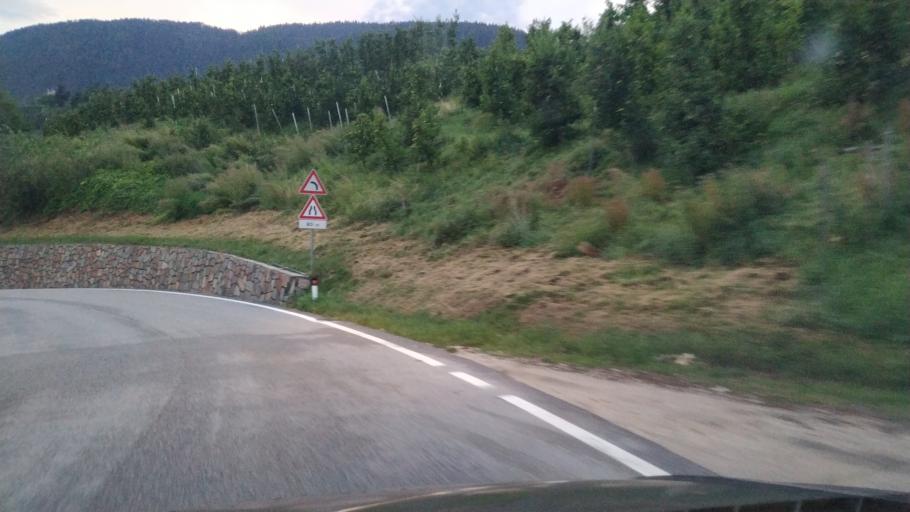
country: IT
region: Trentino-Alto Adige
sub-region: Provincia di Trento
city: Brez
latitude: 46.4379
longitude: 11.1094
